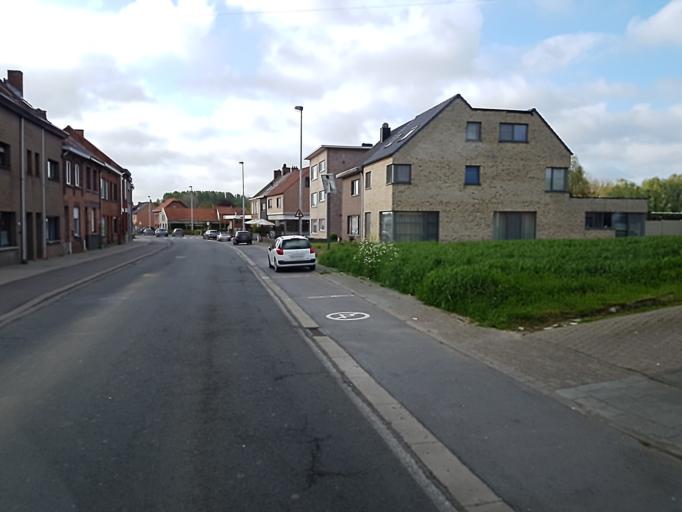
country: BE
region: Flanders
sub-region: Provincie Oost-Vlaanderen
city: Temse
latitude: 51.1332
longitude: 4.1911
